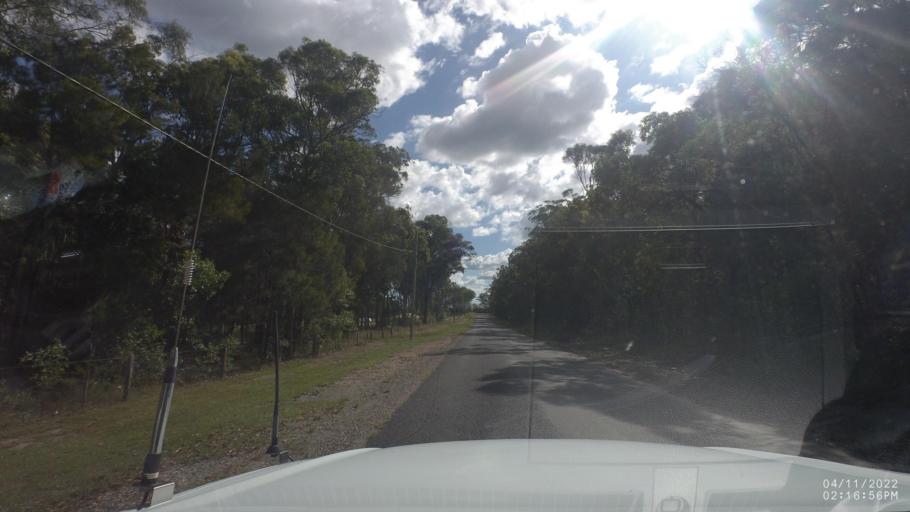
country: AU
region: Queensland
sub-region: Logan
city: Windaroo
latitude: -27.7525
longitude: 153.1454
